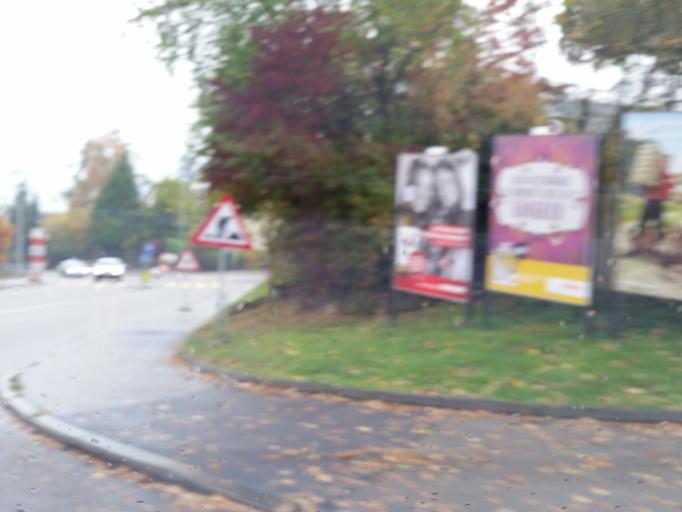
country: CH
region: Zurich
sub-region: Bezirk Zuerich
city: Zuerich (Kreis 10)
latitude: 47.4048
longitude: 8.5042
